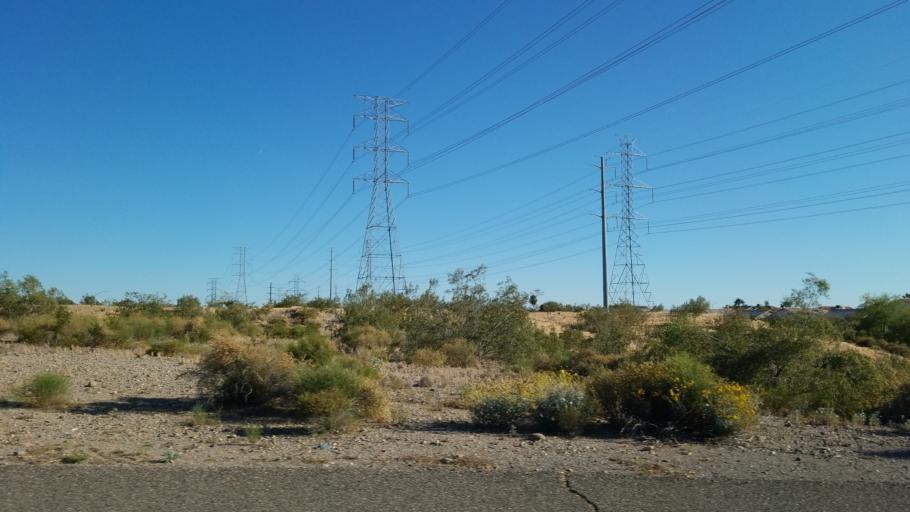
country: US
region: Arizona
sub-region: Maricopa County
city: Youngtown
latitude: 33.5654
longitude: -112.3001
